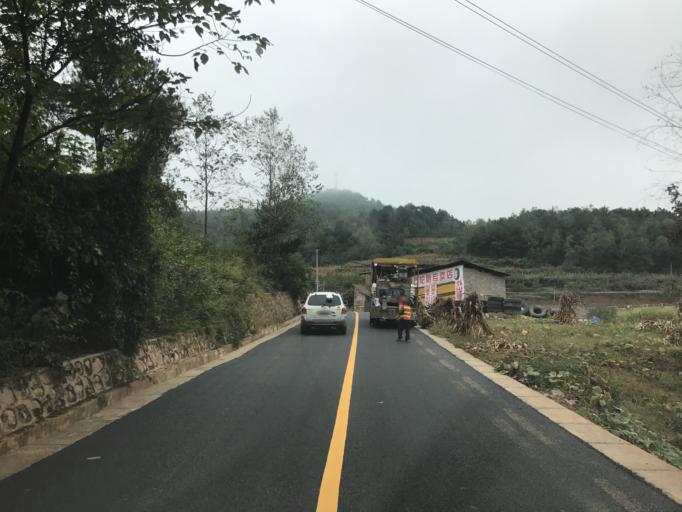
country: CN
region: Guizhou Sheng
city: Supu
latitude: 26.7369
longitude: 106.4368
